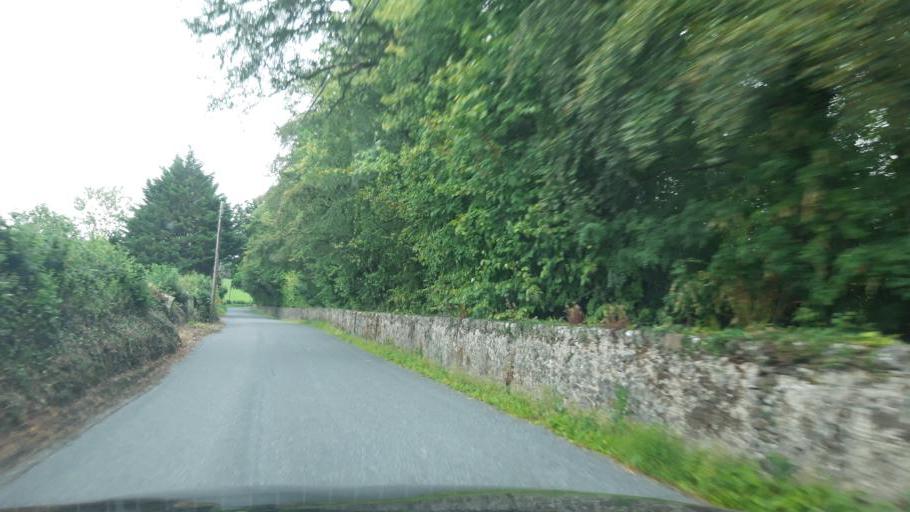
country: IE
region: Leinster
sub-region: Kilkenny
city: Ballyragget
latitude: 52.7266
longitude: -7.3994
